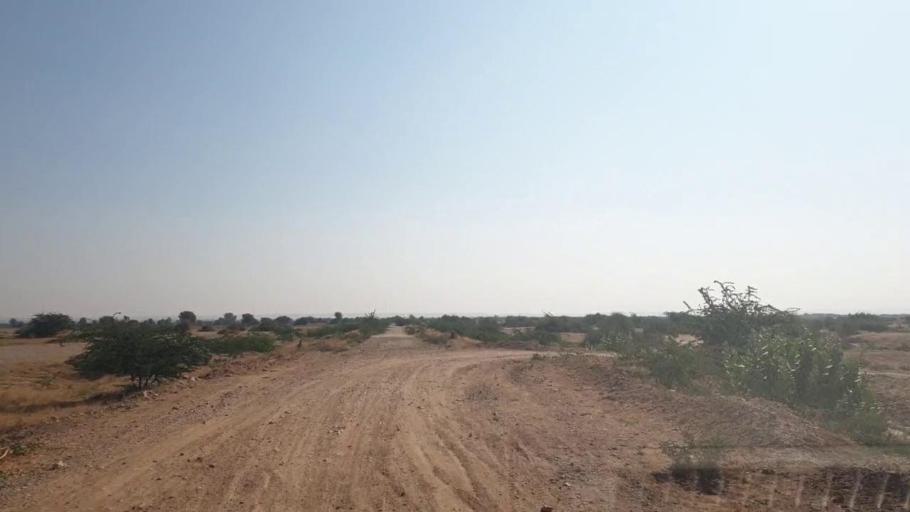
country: PK
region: Sindh
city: Gharo
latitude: 25.1413
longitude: 67.7320
